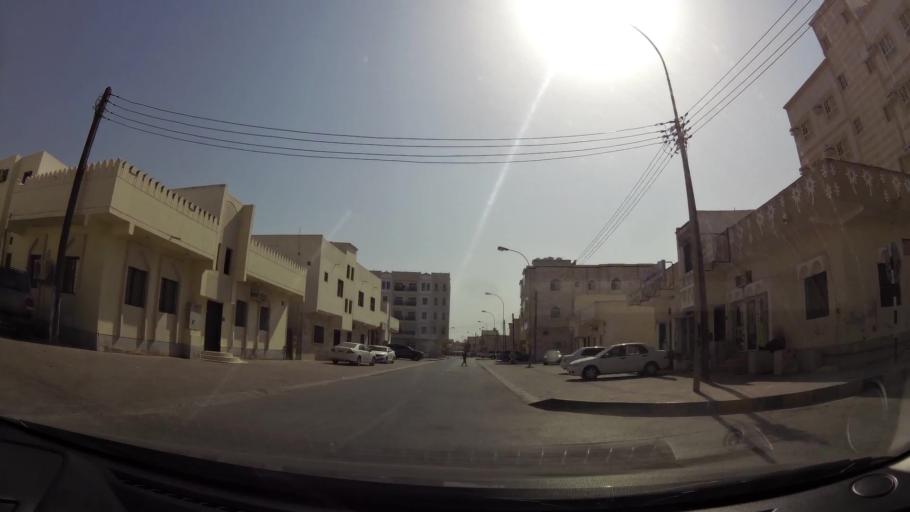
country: OM
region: Zufar
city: Salalah
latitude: 17.0032
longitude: 54.0505
